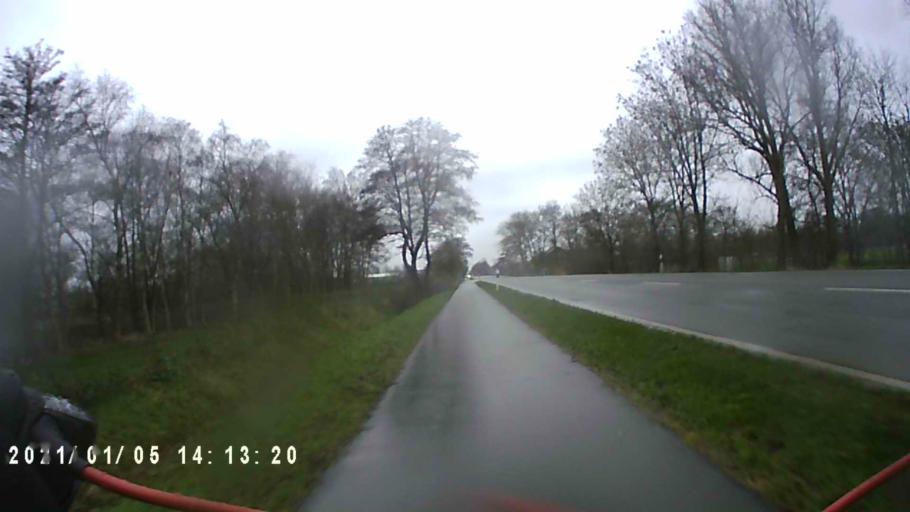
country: DE
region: Lower Saxony
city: Weener
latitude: 53.1715
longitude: 7.3239
